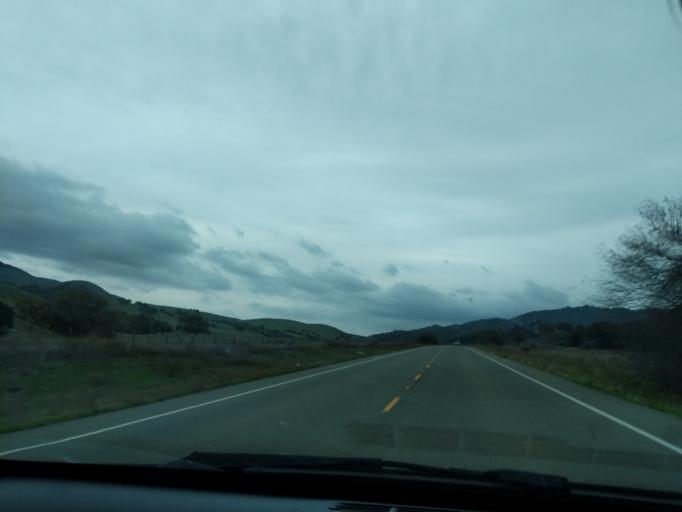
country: US
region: California
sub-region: Monterey County
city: Soledad
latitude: 36.6300
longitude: -121.2259
